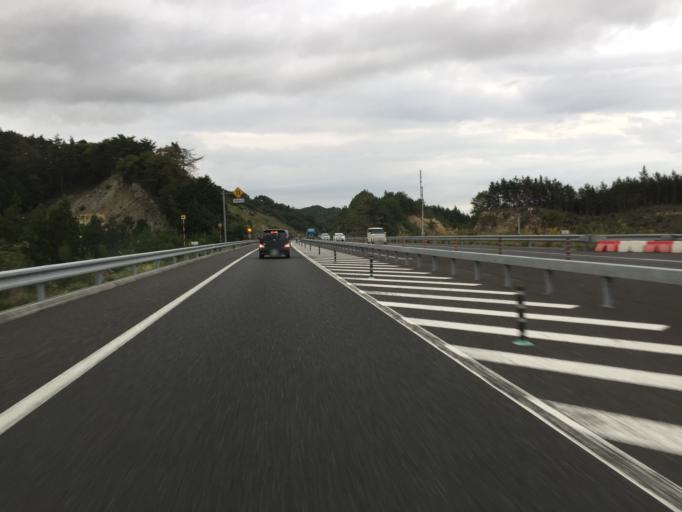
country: JP
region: Fukushima
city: Namie
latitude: 37.6802
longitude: 140.9173
